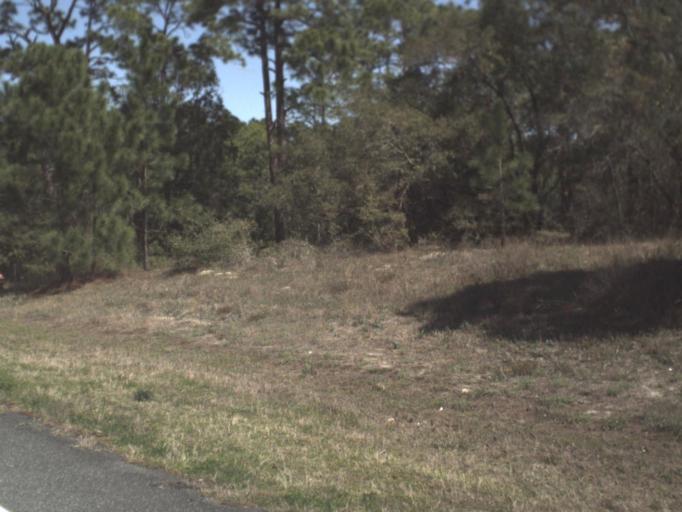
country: US
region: Florida
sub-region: Wakulla County
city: Crawfordville
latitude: 29.9977
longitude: -84.3983
